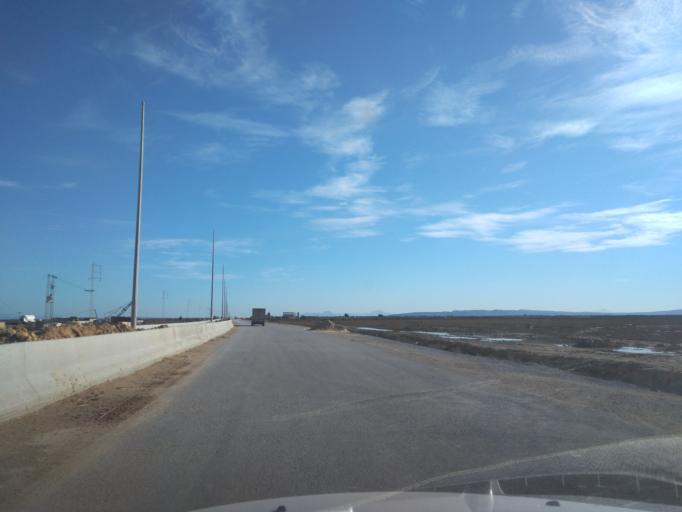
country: TN
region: Ariana
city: Qal'at al Andalus
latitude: 37.0470
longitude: 10.1252
